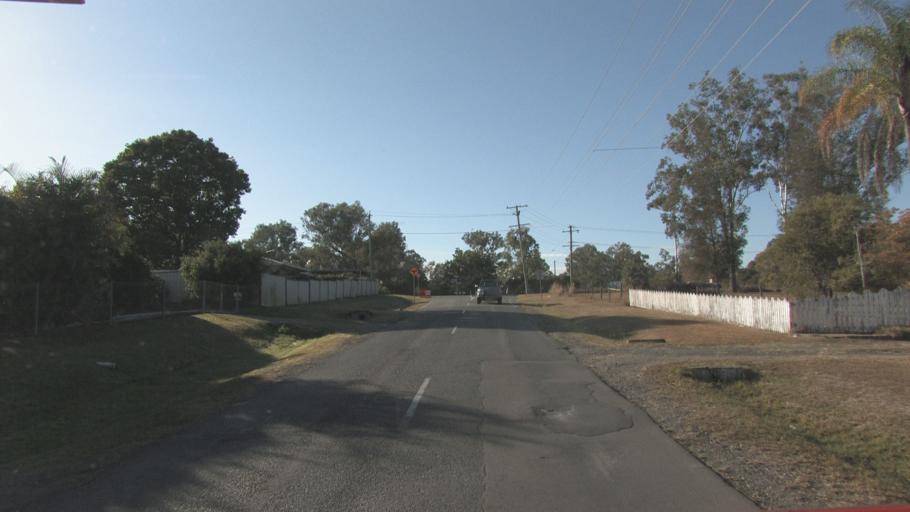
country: AU
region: Queensland
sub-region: Logan
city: Cedar Vale
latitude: -27.8353
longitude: 153.0313
